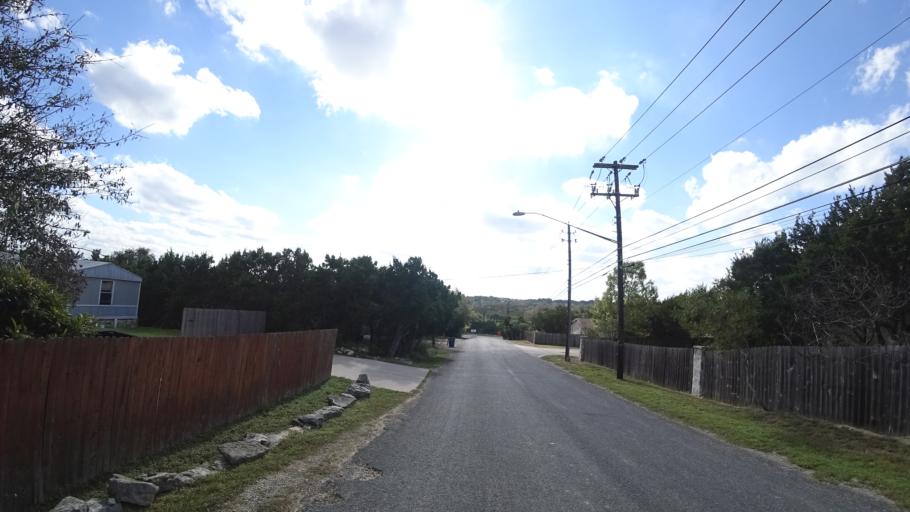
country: US
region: Texas
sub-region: Travis County
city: Barton Creek
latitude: 30.2481
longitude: -97.8823
